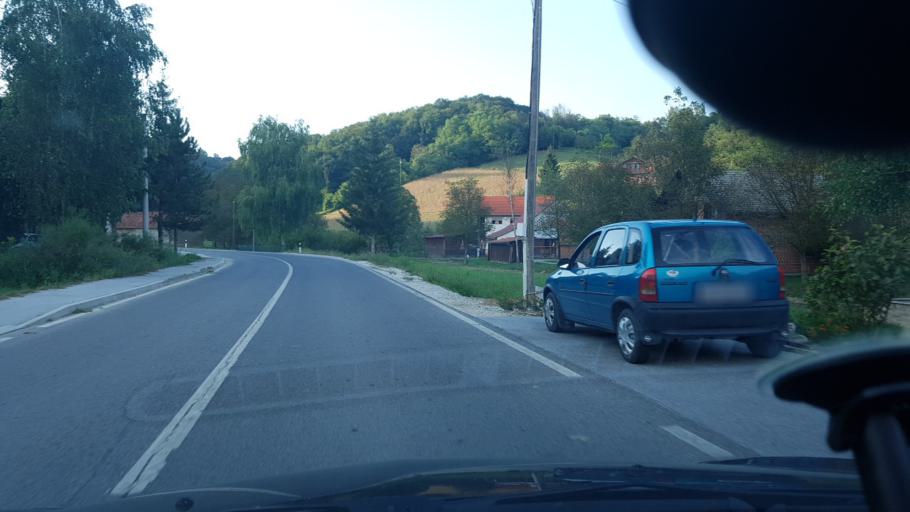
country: HR
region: Krapinsko-Zagorska
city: Pregrada
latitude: 46.1498
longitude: 15.7936
